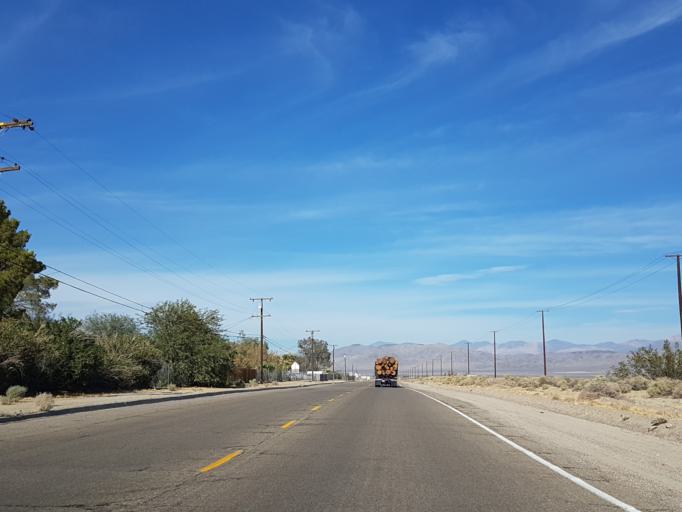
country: US
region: California
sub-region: San Bernardino County
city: Searles Valley
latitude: 35.7923
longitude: -117.3574
